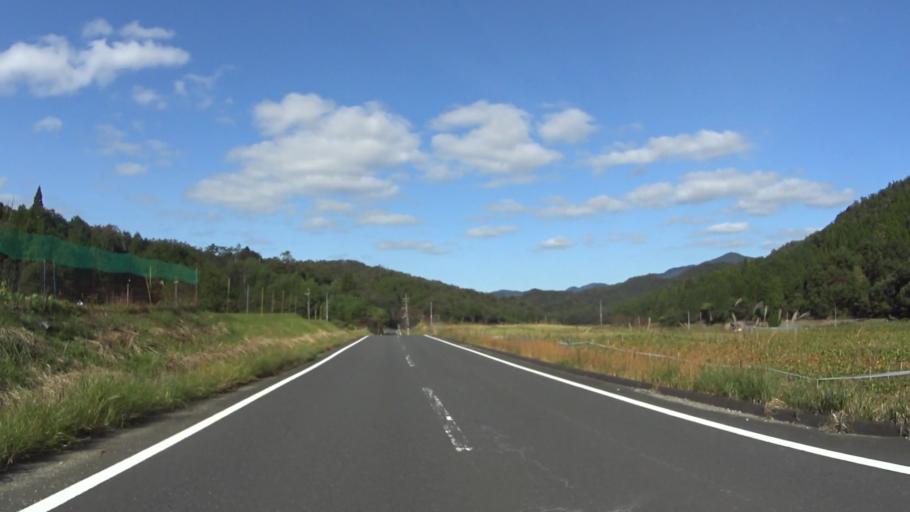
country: JP
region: Hyogo
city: Toyooka
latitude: 35.5499
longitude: 134.9775
